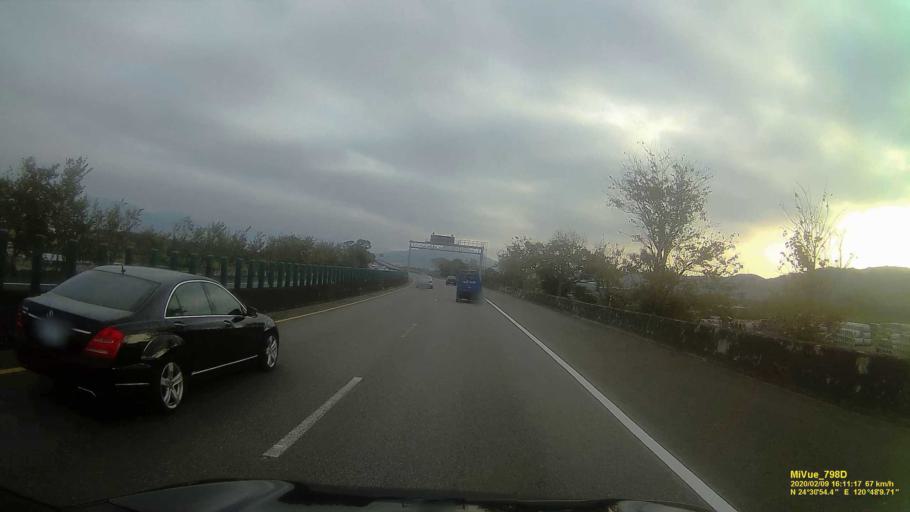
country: TW
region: Taiwan
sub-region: Miaoli
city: Miaoli
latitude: 24.5147
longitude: 120.8026
